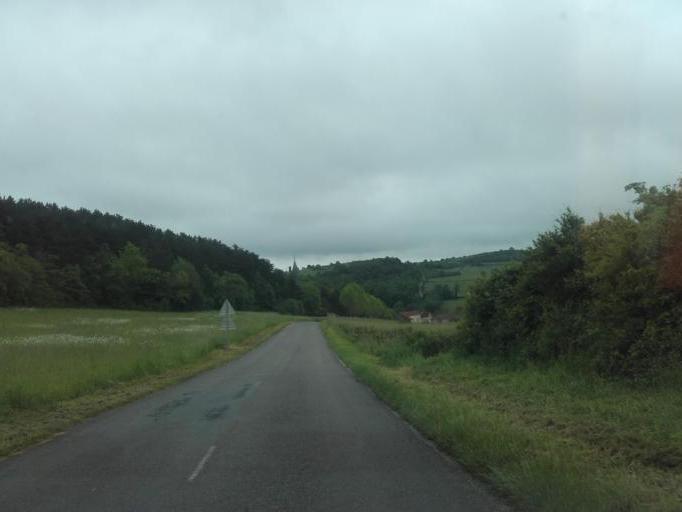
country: FR
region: Bourgogne
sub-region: Departement de la Cote-d'Or
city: Nolay
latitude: 46.9631
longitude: 4.6802
